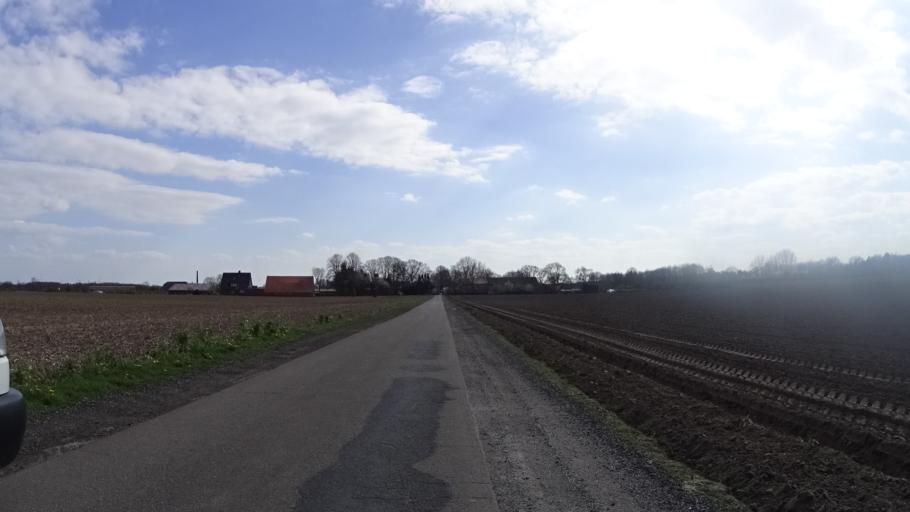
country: DE
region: Lower Saxony
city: Lehe
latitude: 53.0339
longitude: 7.3216
